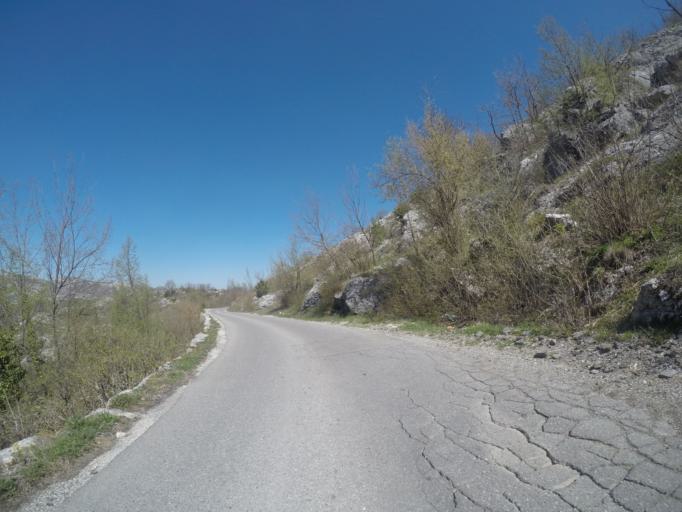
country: ME
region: Cetinje
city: Cetinje
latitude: 42.4449
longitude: 18.8739
